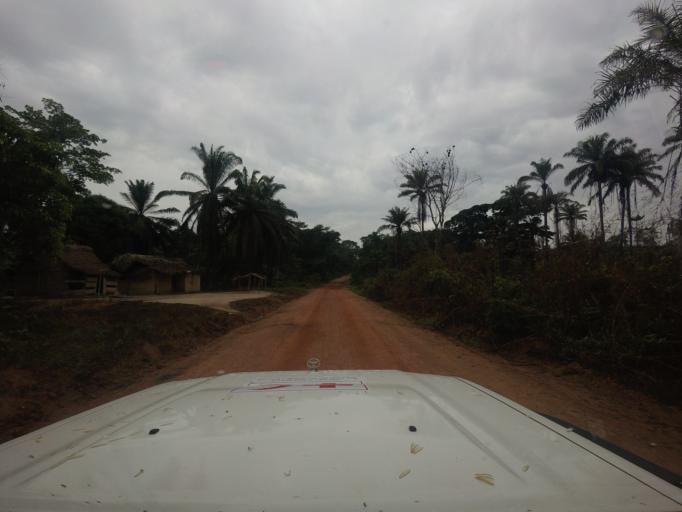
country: LR
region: Lofa
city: Voinjama
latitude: 8.3754
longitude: -9.8557
